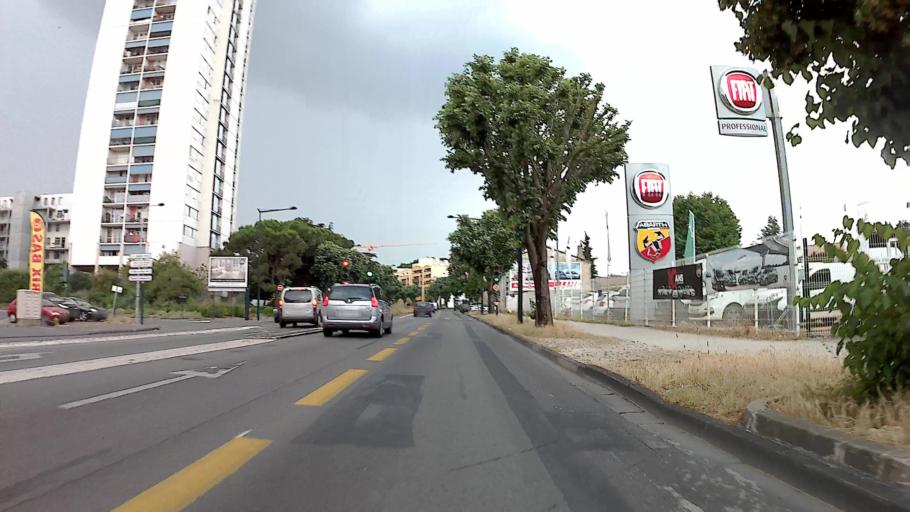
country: FR
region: Aquitaine
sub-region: Departement de la Gironde
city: Le Bouscat
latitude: 44.8621
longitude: -0.5857
